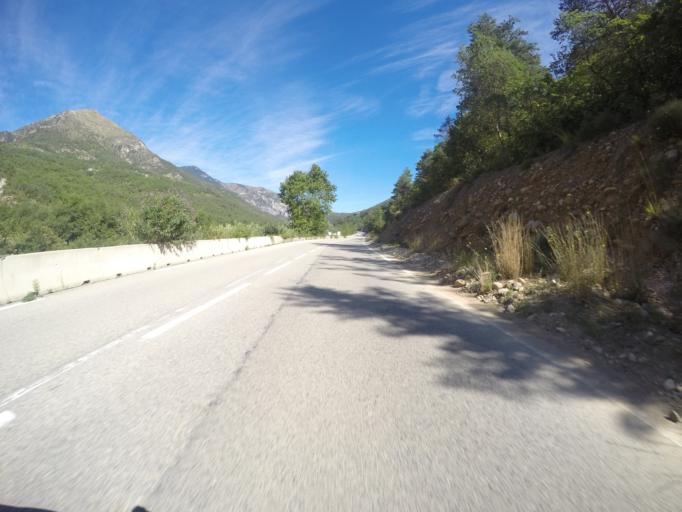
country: FR
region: Provence-Alpes-Cote d'Azur
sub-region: Departement des Alpes-Maritimes
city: Gilette
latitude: 43.9518
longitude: 7.1598
